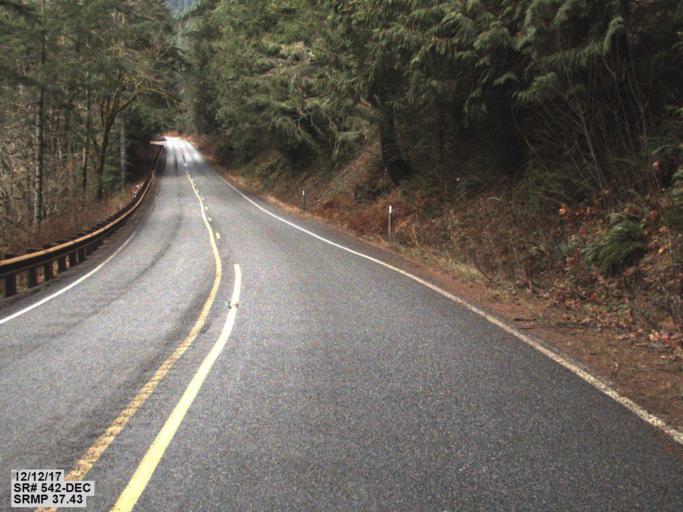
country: CA
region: British Columbia
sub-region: Fraser Valley Regional District
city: Chilliwack
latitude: 48.9033
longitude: -121.8715
